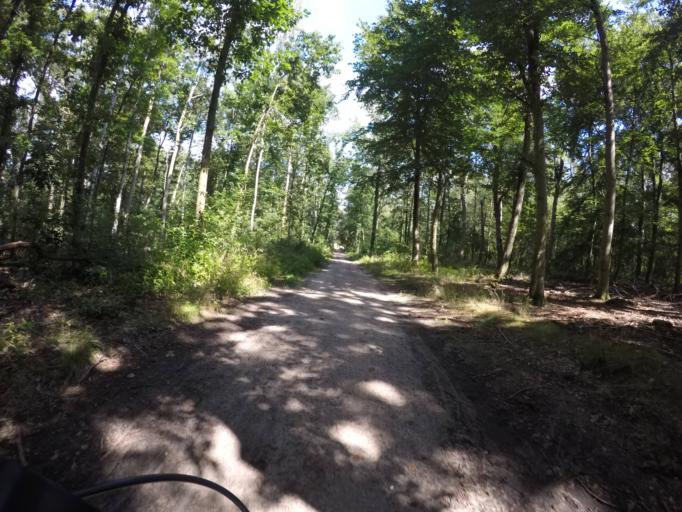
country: DE
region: Brandenburg
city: Potsdam
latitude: 52.3935
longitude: 13.0084
